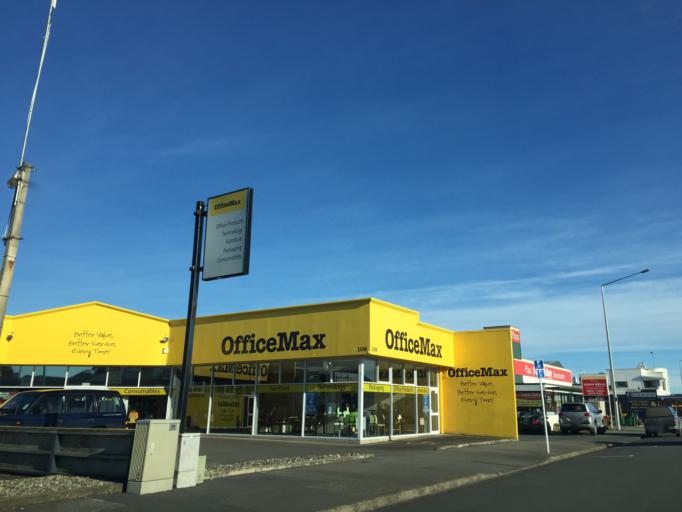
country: NZ
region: Southland
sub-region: Invercargill City
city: Invercargill
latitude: -46.4085
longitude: 168.3553
